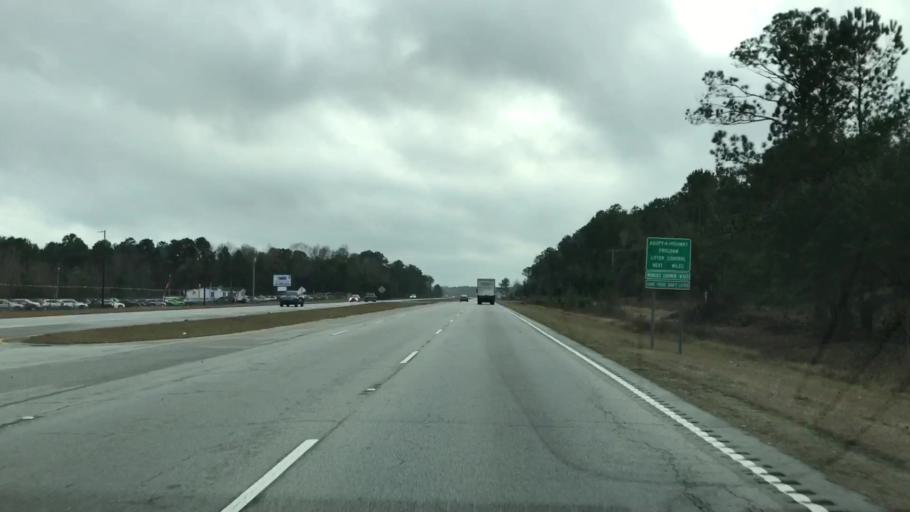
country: US
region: South Carolina
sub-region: Berkeley County
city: Moncks Corner
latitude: 33.1795
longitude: -80.0194
